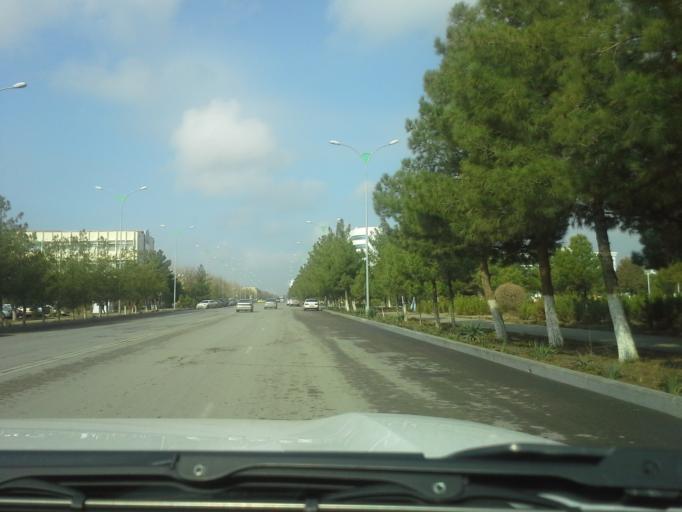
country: TM
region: Mary
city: Mary
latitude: 37.5908
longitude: 61.8402
